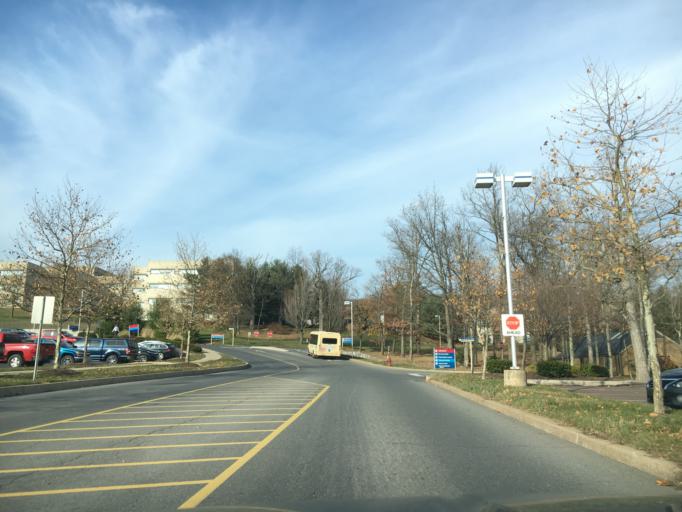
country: US
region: Pennsylvania
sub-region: Montour County
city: Danville
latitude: 40.9691
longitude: -76.6015
